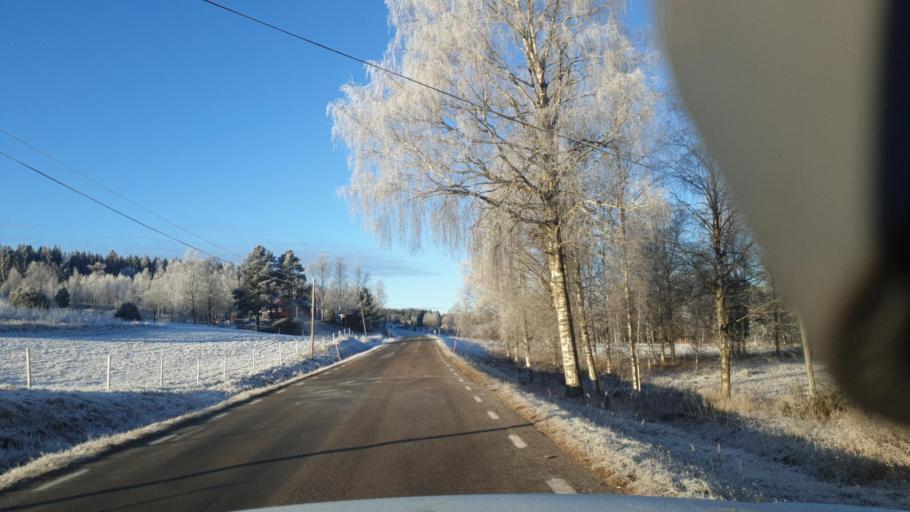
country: SE
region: Vaermland
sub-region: Arvika Kommun
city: Arvika
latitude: 59.7780
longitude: 12.7791
